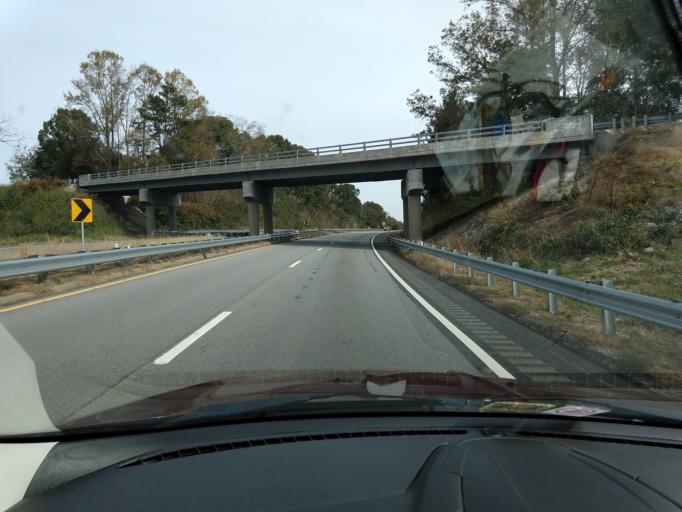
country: US
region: Virginia
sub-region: Pittsylvania County
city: Chatham
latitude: 36.8065
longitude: -79.3926
